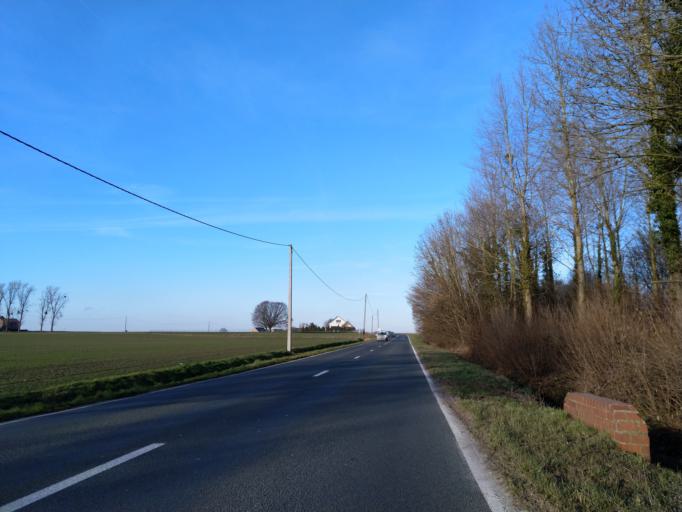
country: BE
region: Wallonia
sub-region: Province du Hainaut
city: Frameries
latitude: 50.3743
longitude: 3.8969
